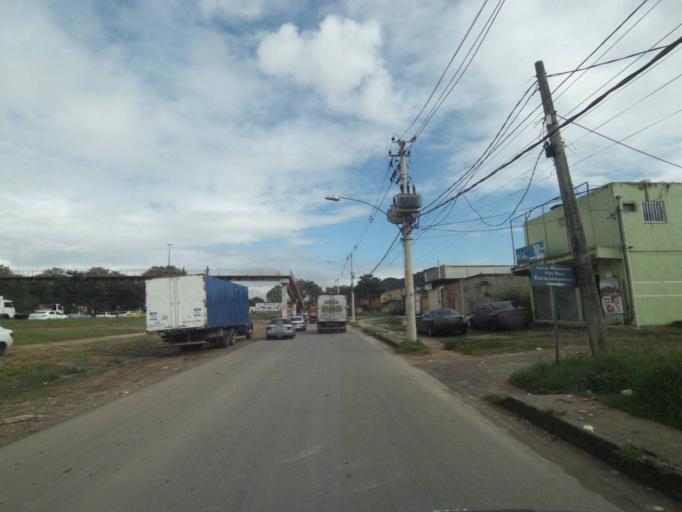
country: BR
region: Rio de Janeiro
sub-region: Nilopolis
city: Nilopolis
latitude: -22.8546
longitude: -43.4875
